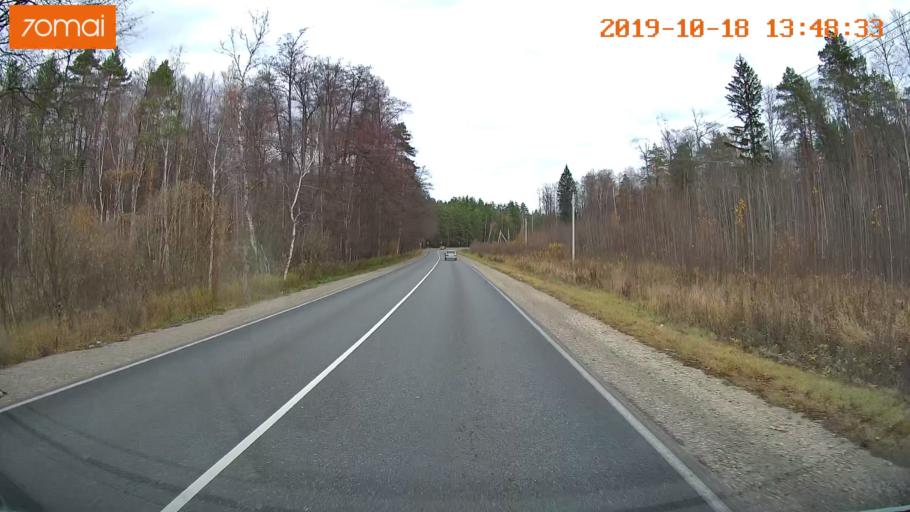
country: RU
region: Moskovskaya
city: Radovitskiy
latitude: 54.9888
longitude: 39.9574
